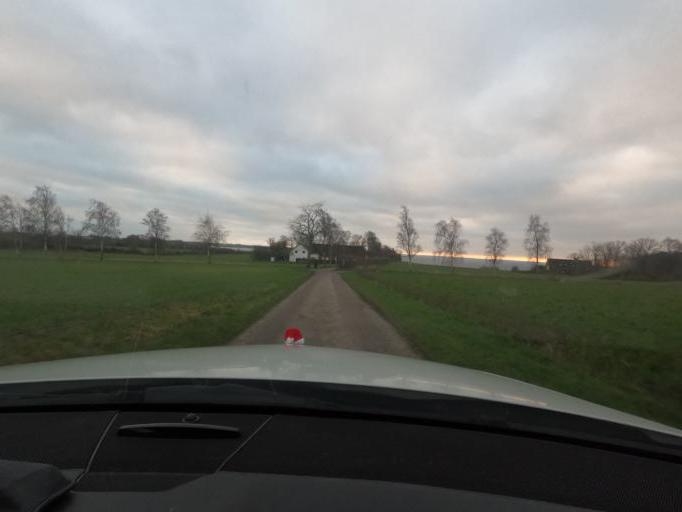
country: DK
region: South Denmark
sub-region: Sonderborg Kommune
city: Horuphav
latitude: 54.9000
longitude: 9.8532
